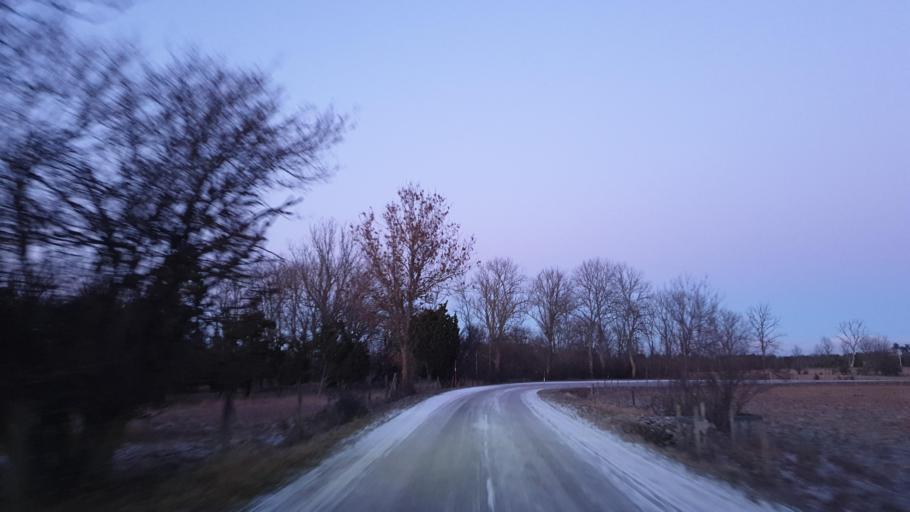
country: SE
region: Gotland
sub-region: Gotland
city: Slite
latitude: 57.4214
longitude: 18.8219
